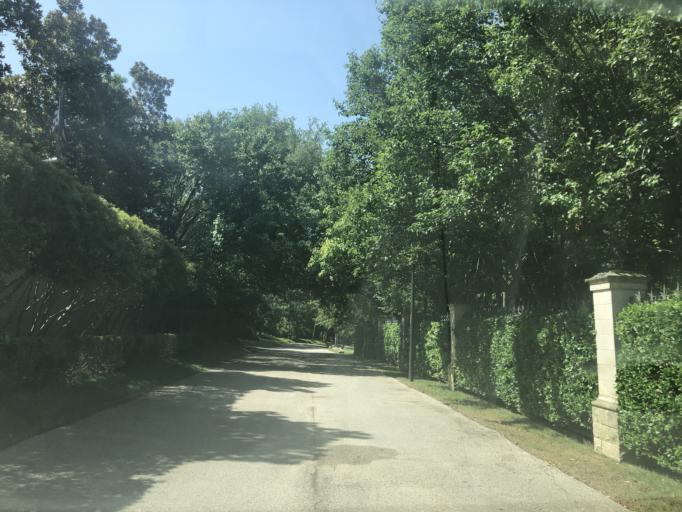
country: US
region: Texas
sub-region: Dallas County
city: University Park
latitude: 32.8748
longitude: -96.8196
